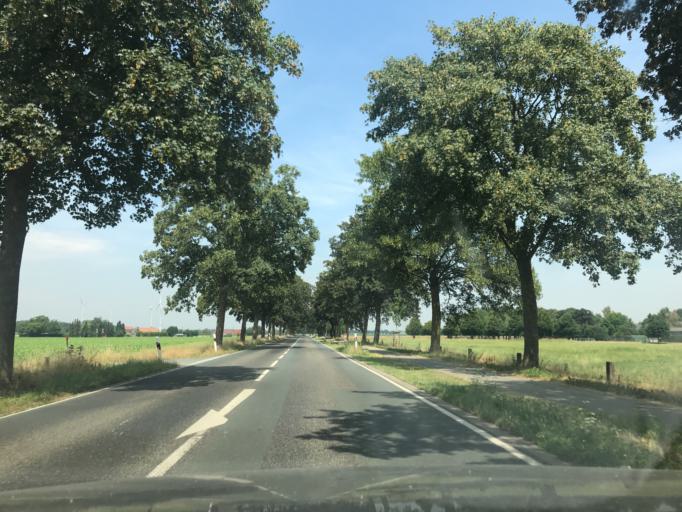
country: DE
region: North Rhine-Westphalia
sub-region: Regierungsbezirk Dusseldorf
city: Rheurdt
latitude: 51.4671
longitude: 6.4187
